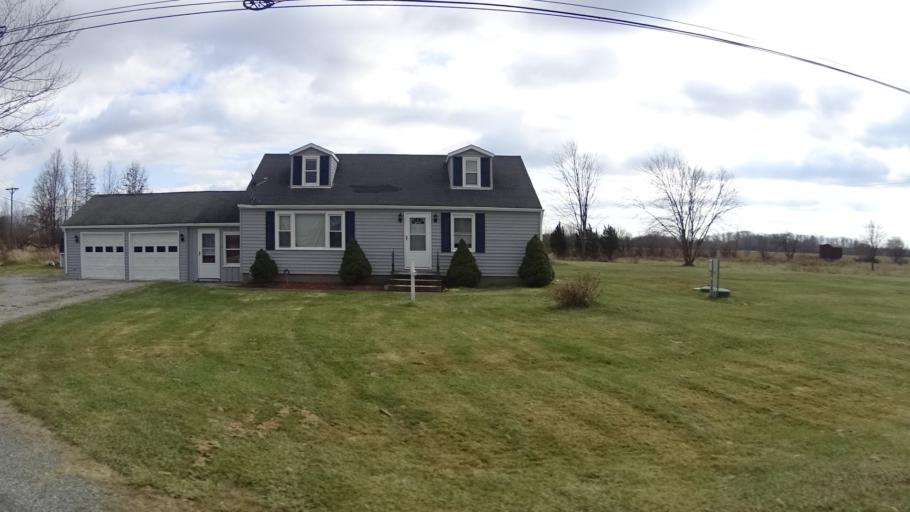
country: US
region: Ohio
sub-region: Lorain County
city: Oberlin
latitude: 41.2791
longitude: -82.1878
